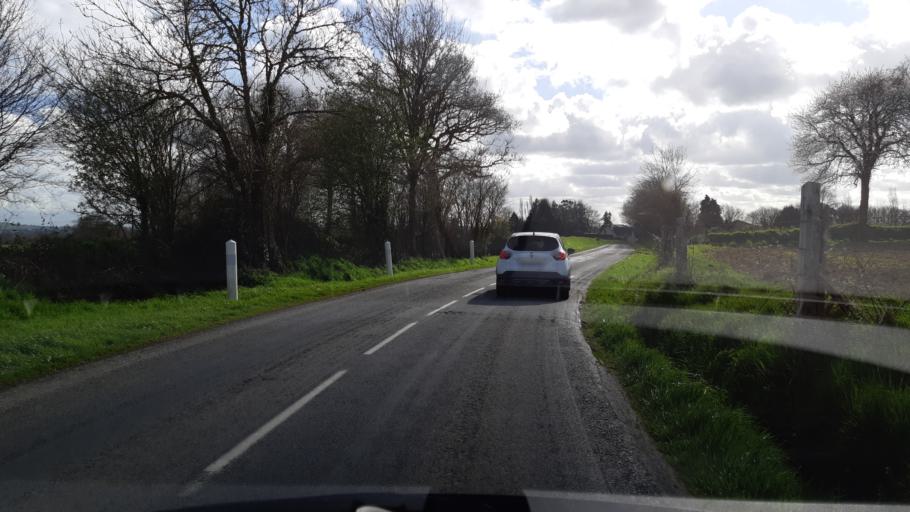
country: FR
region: Lower Normandy
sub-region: Departement de la Manche
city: Percy
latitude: 49.0162
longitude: -1.1638
